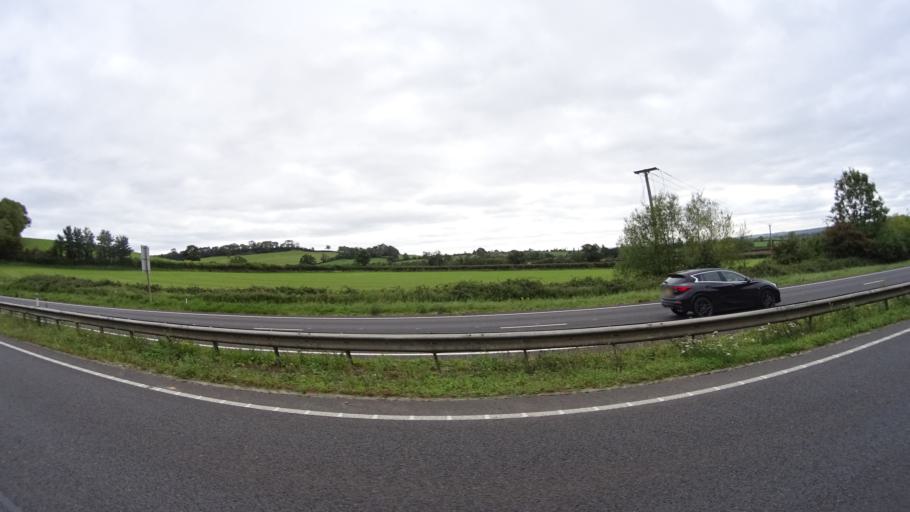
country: GB
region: England
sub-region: Somerset
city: Wincanton
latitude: 51.0551
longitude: -2.3965
